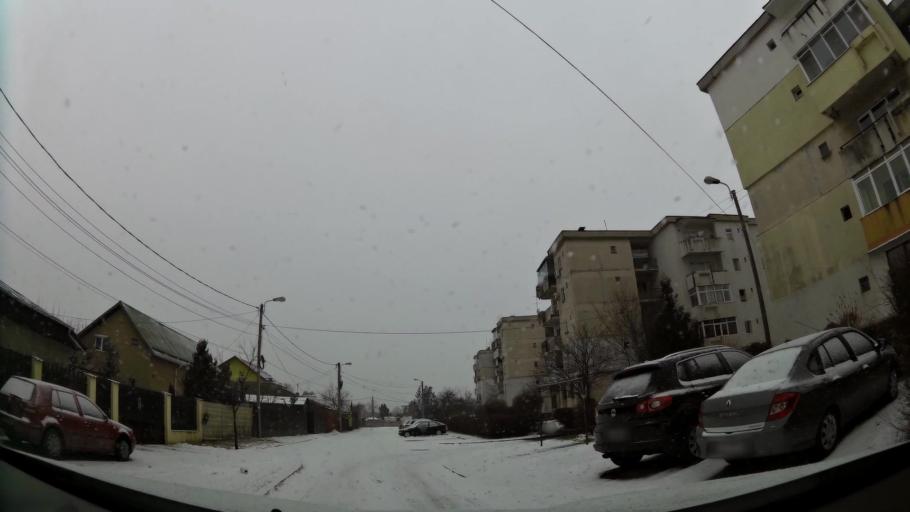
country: RO
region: Prahova
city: Ploiesti
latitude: 44.9286
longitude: 26.0097
